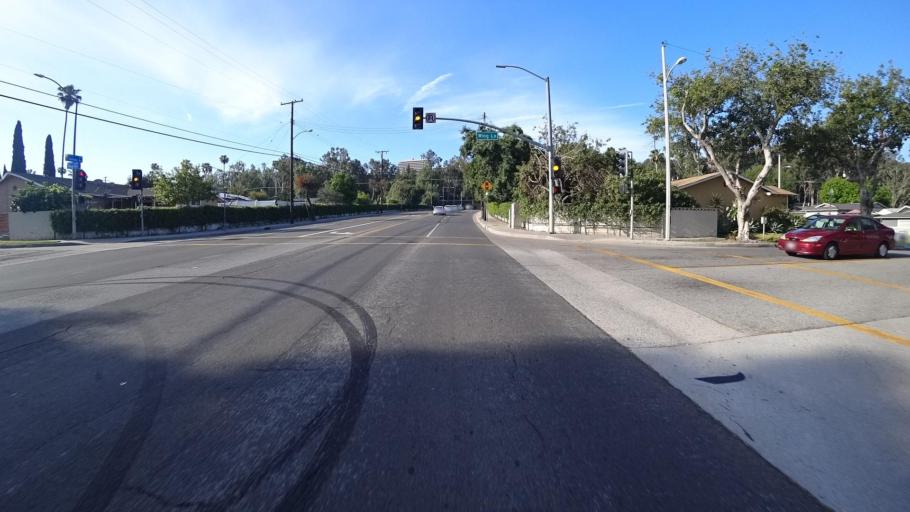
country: US
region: California
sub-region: Los Angeles County
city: La Puente
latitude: 34.0279
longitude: -117.9272
